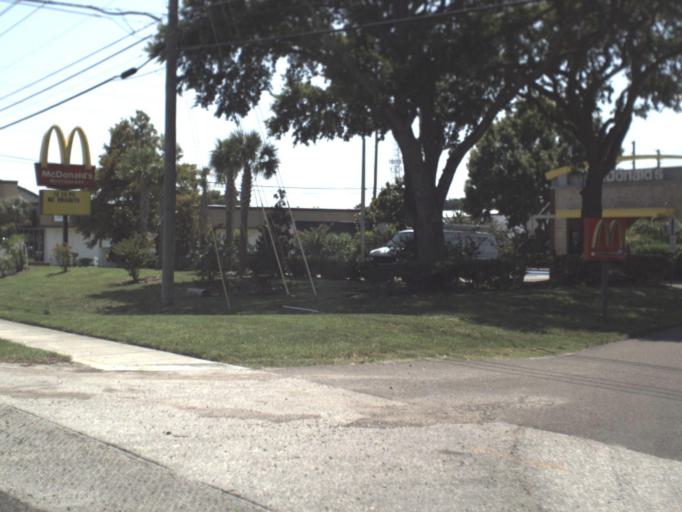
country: US
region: Florida
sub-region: Pinellas County
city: Saint George
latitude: 28.0449
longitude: -82.7386
